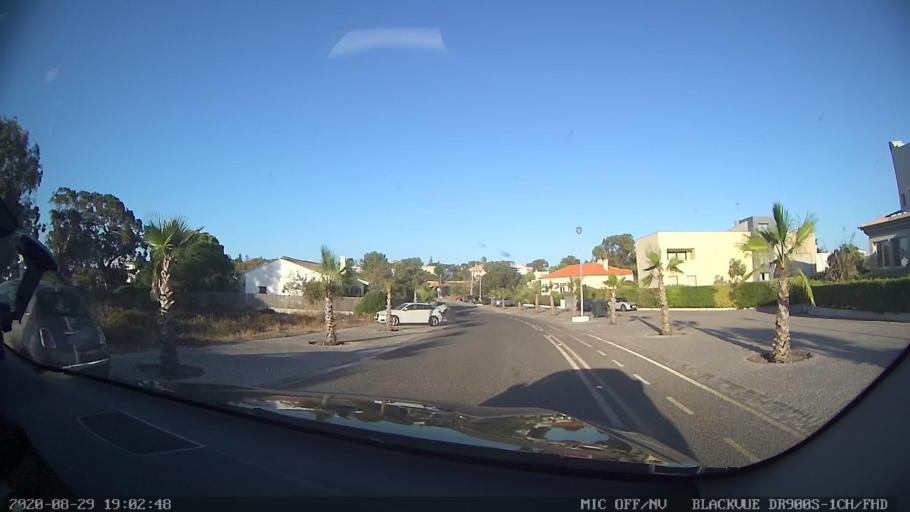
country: PT
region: Setubal
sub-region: Setubal
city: Setubal
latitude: 38.4533
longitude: -8.8593
